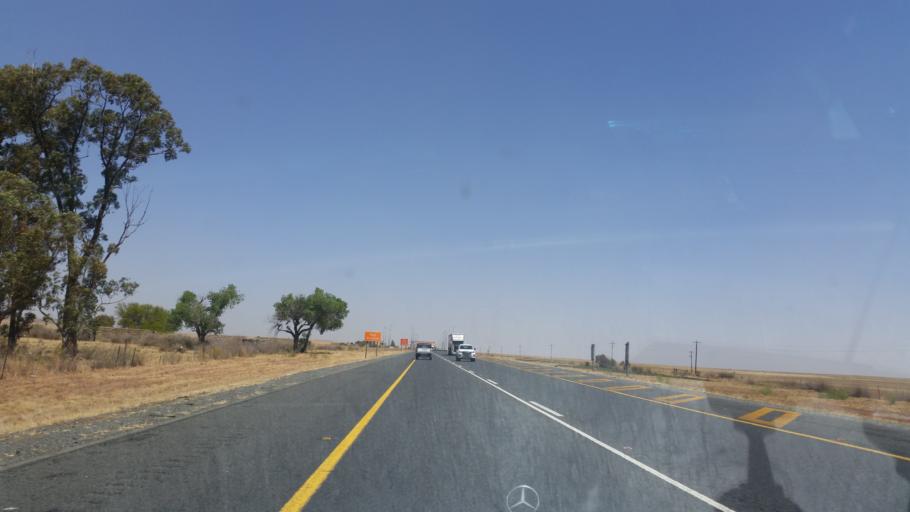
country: ZA
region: Orange Free State
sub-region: Lejweleputswa District Municipality
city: Brandfort
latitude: -28.7929
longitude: 26.6982
